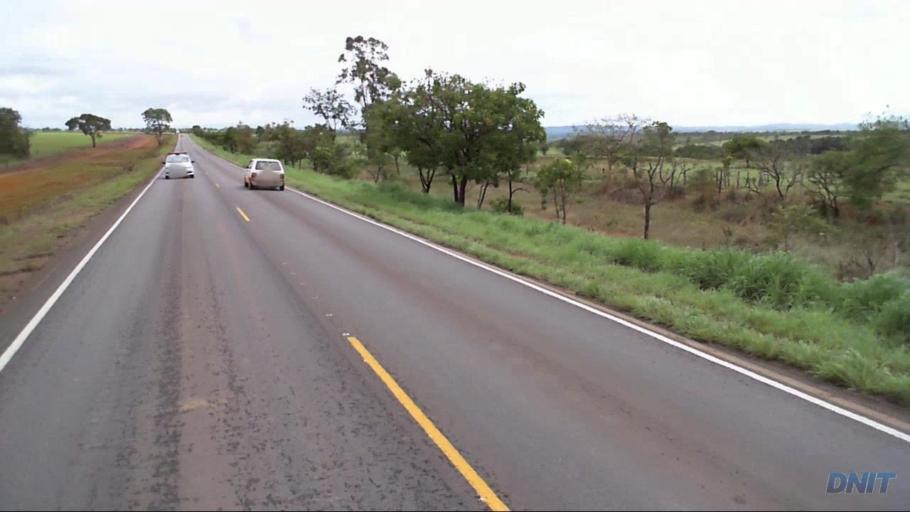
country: BR
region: Goias
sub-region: Padre Bernardo
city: Padre Bernardo
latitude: -15.3150
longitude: -48.2284
